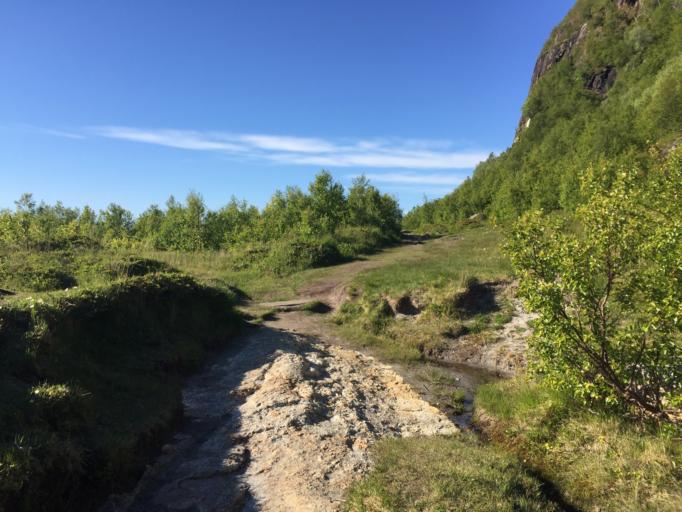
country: NO
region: Nordland
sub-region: Bodo
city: Loding
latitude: 67.4154
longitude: 14.6329
